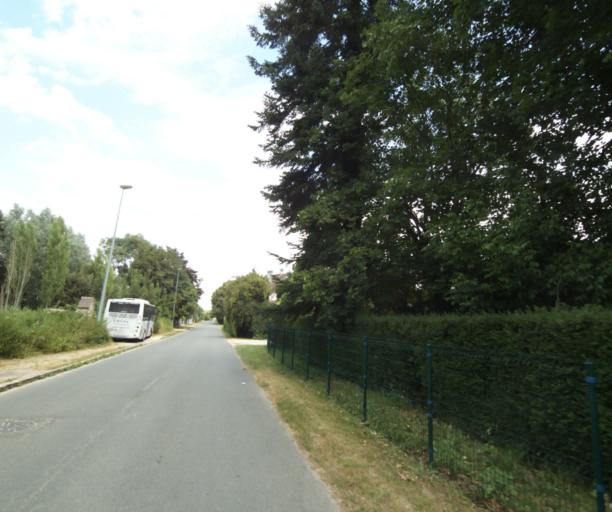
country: FR
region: Ile-de-France
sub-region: Departement de Seine-et-Marne
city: Hericy
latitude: 48.4526
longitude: 2.7592
